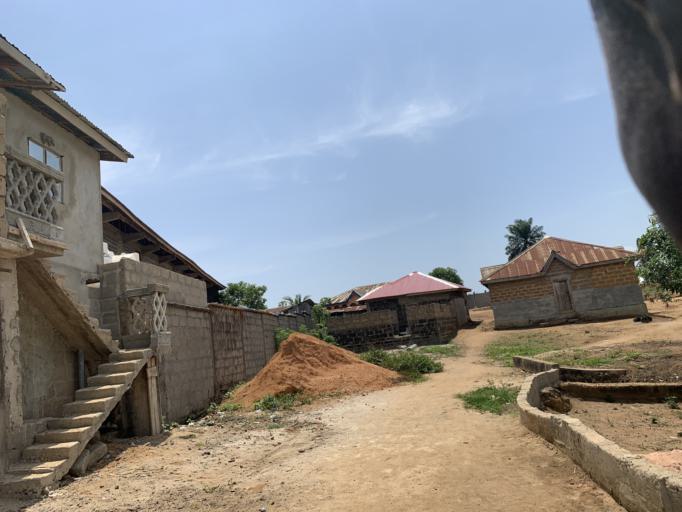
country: SL
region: Western Area
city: Waterloo
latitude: 8.3423
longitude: -13.0366
